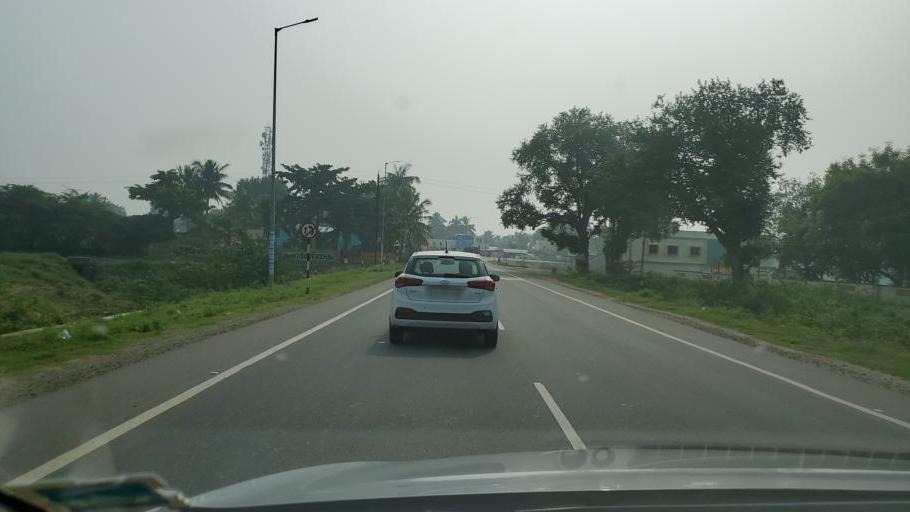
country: IN
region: Tamil Nadu
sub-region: Ariyalur
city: Ariyalur
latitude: 11.2371
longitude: 79.0204
